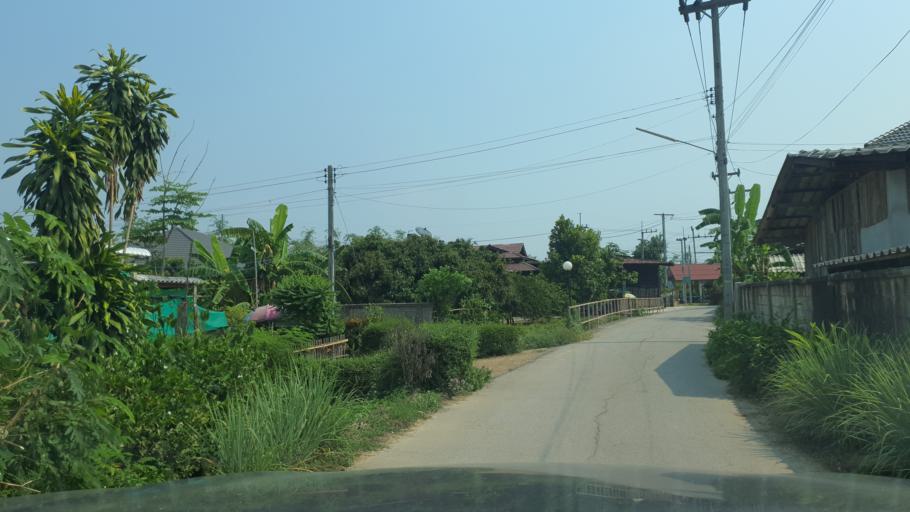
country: TH
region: Lamphun
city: Lamphun
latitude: 18.6407
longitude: 98.9908
